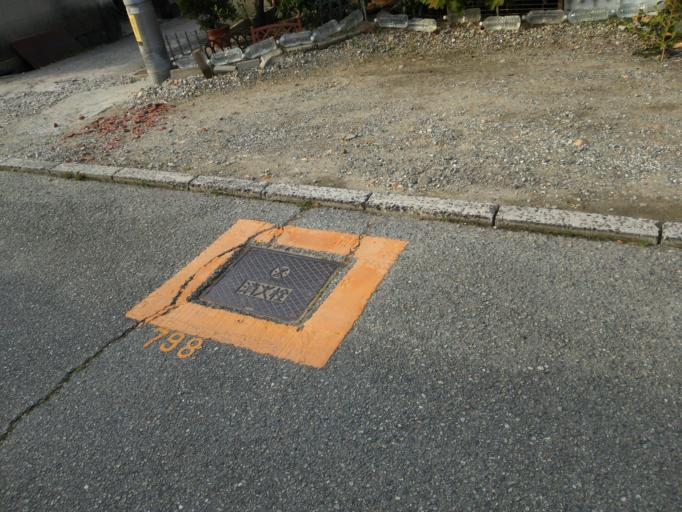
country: JP
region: Hyogo
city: Amagasaki
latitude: 34.7389
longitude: 135.4354
